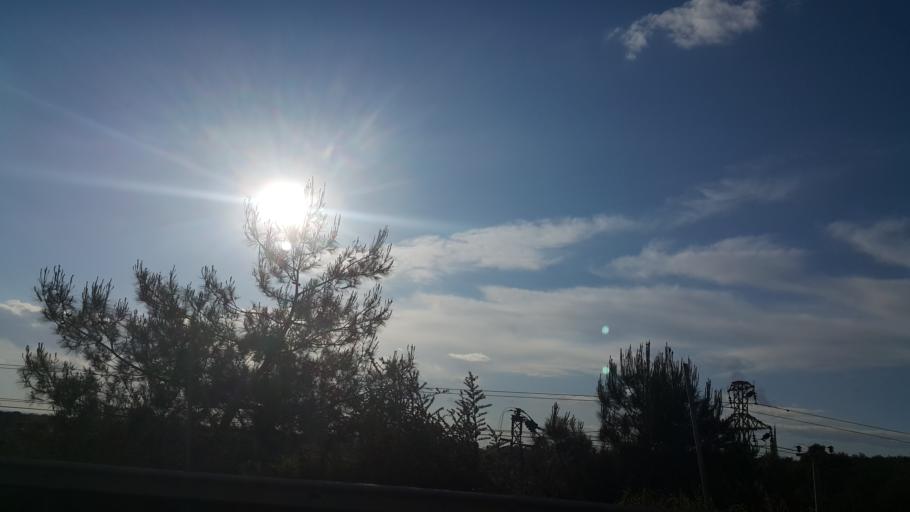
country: TR
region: Hatay
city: Denizciler
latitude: 36.7018
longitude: 36.2171
